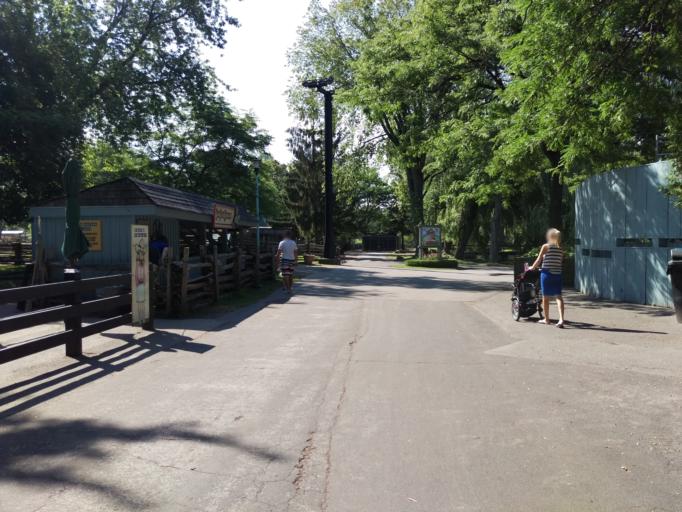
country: CA
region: Ontario
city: Toronto
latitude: 43.6203
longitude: -79.3720
